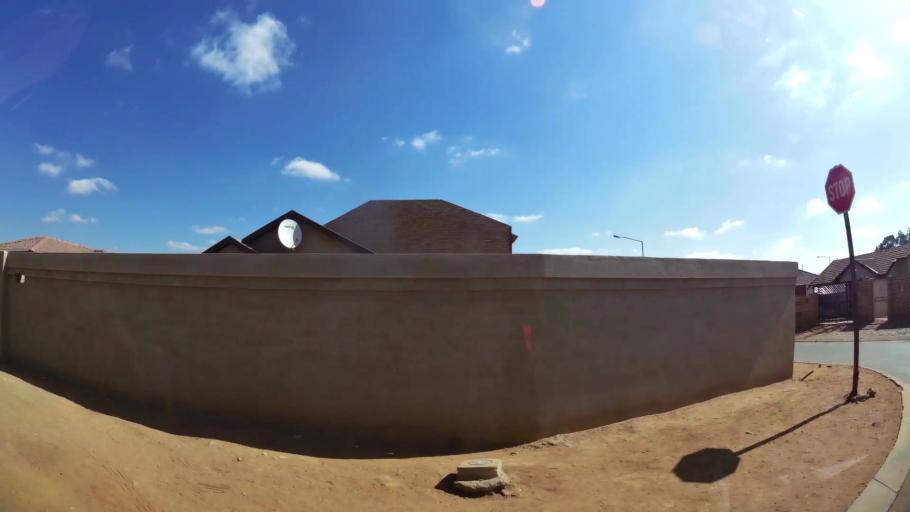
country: ZA
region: Gauteng
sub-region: West Rand District Municipality
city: Krugersdorp
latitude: -26.1504
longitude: 27.7750
